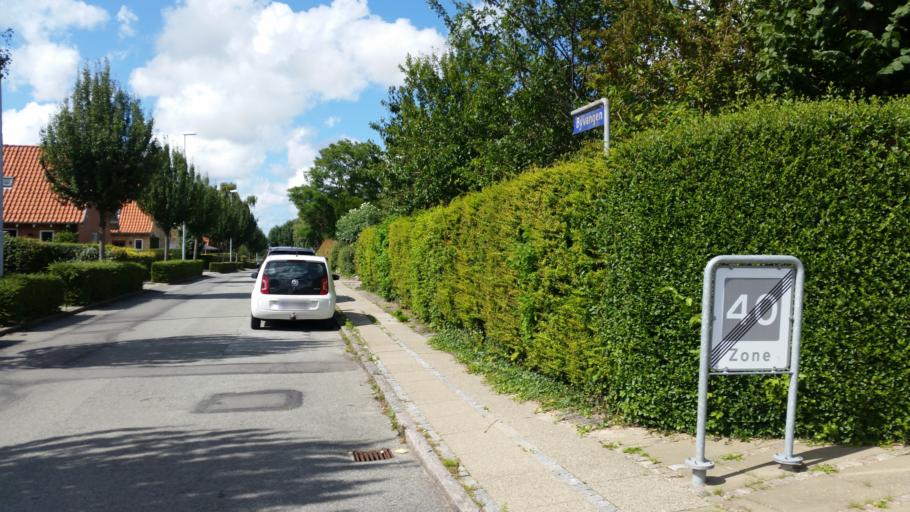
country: DK
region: North Denmark
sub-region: Thisted Kommune
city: Thisted
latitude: 56.9582
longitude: 8.6966
